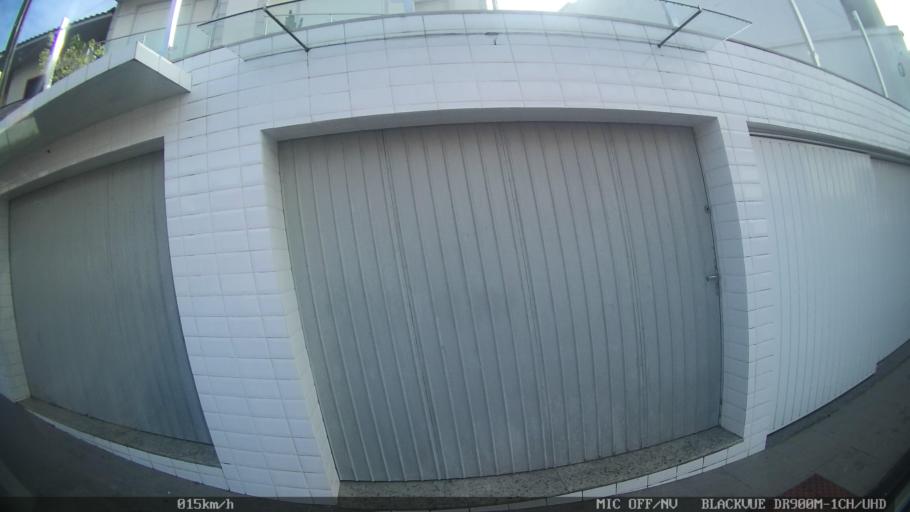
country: BR
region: Santa Catarina
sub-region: Sao Jose
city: Campinas
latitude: -27.6138
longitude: -48.6310
